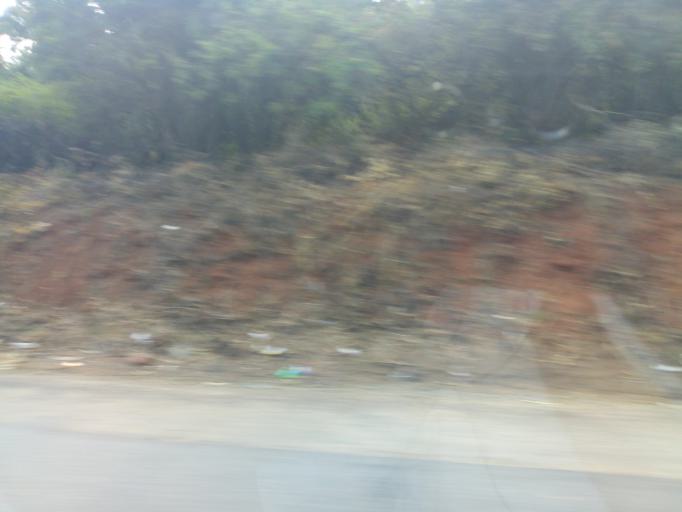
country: KE
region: Kiambu
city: Limuru
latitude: -1.0354
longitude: 36.6011
